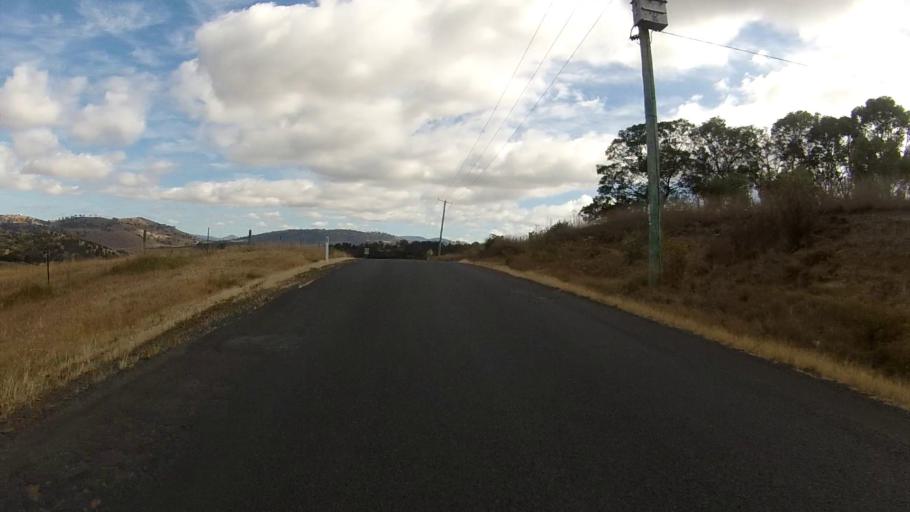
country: AU
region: Tasmania
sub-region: Brighton
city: Old Beach
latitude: -42.7582
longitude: 147.3045
